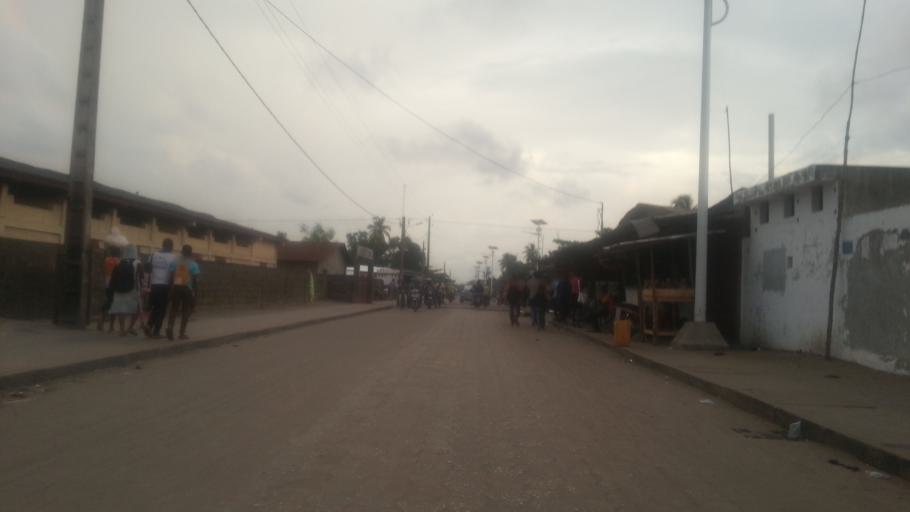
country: BJ
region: Queme
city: Porto-Novo
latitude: 6.3885
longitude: 2.5426
